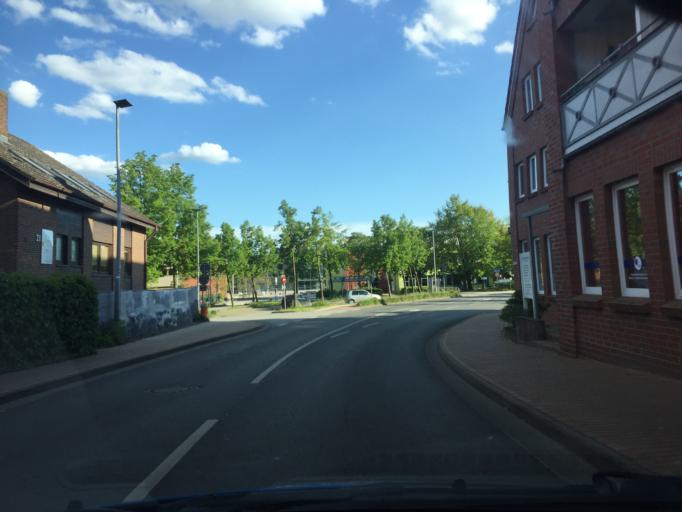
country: DE
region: Lower Saxony
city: Dannenberg
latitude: 53.0983
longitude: 11.0973
